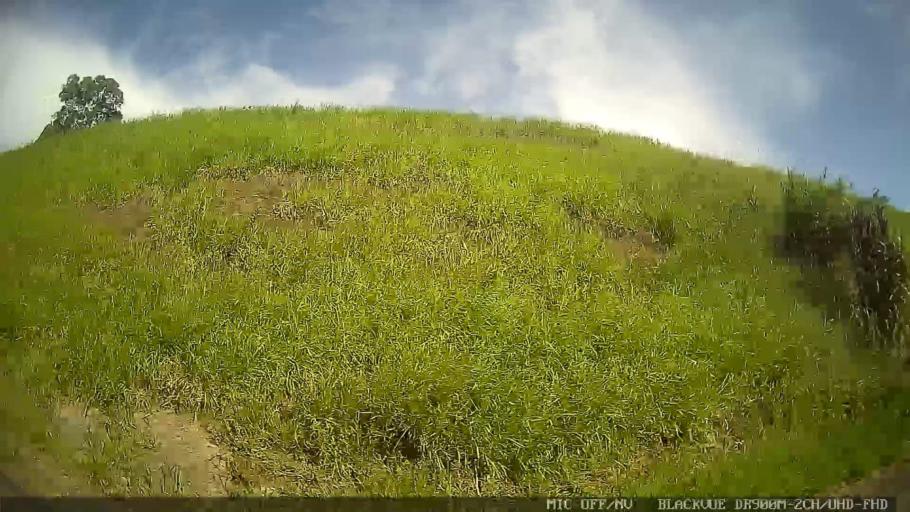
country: BR
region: Sao Paulo
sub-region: Tiete
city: Tiete
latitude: -23.0949
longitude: -47.6873
